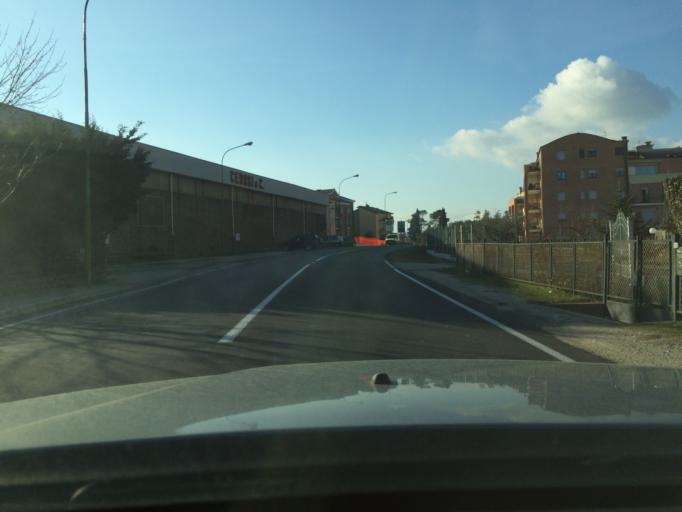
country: IT
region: Umbria
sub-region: Provincia di Terni
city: Amelia
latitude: 42.5554
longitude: 12.4302
